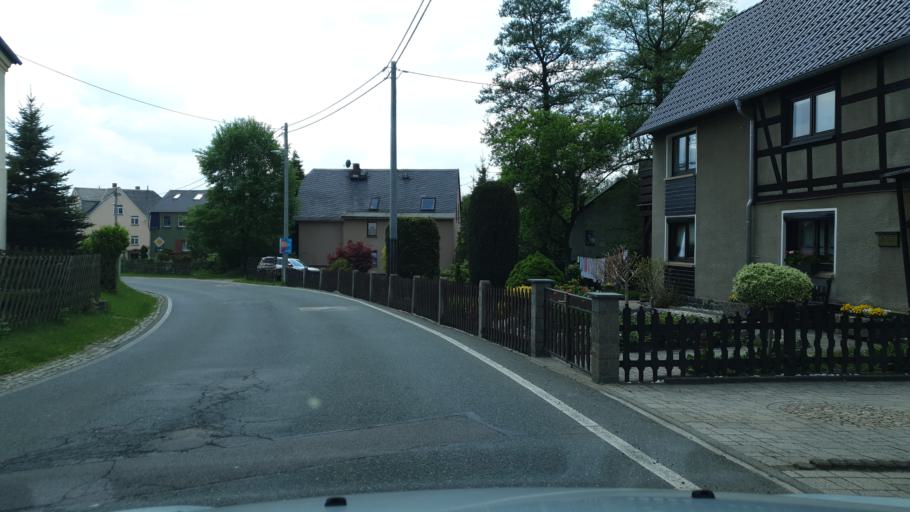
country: DE
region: Saxony
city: Hartenstein
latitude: 50.6771
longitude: 12.6872
